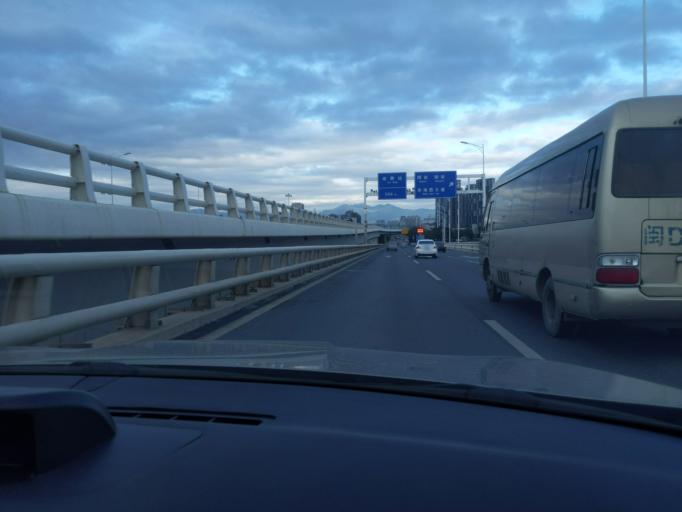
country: CN
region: Fujian
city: Yingcun
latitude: 24.5824
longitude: 118.1126
